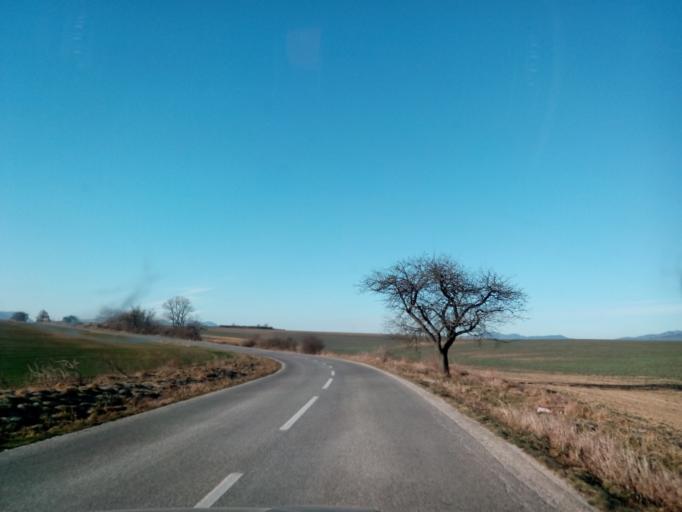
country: SK
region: Kosicky
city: Moldava nad Bodvou
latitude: 48.6872
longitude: 20.9986
